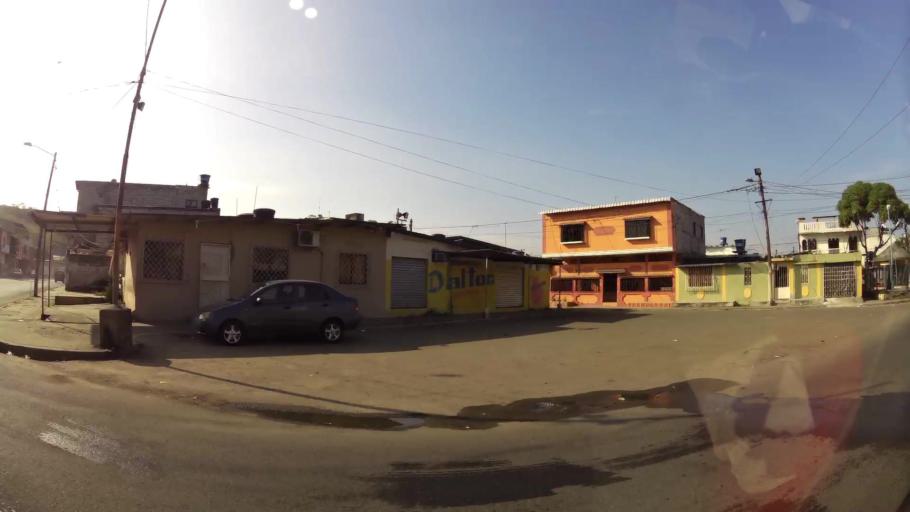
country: EC
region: Guayas
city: Eloy Alfaro
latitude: -2.1739
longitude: -79.8407
